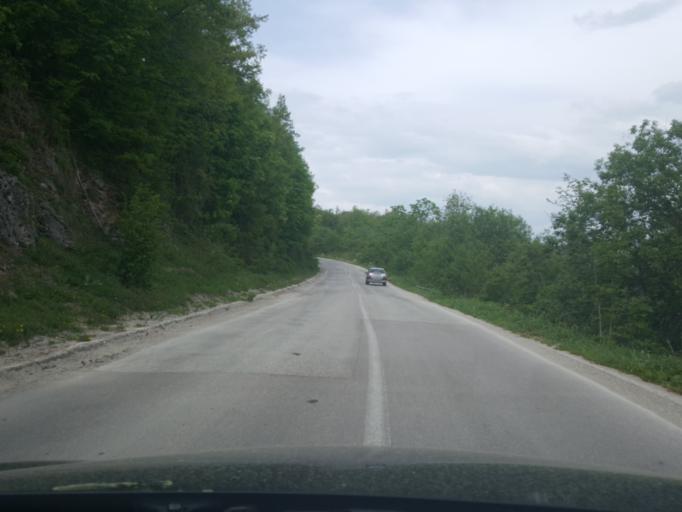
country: RS
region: Central Serbia
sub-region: Zlatiborski Okrug
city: Bajina Basta
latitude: 44.0980
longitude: 19.6718
